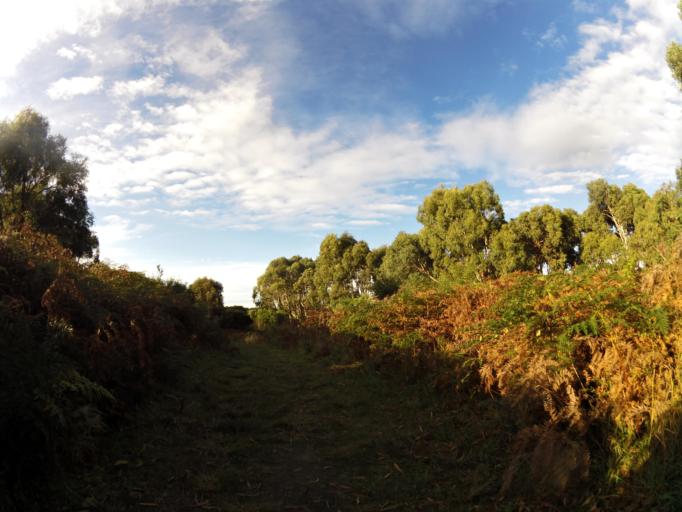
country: AU
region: Victoria
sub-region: Bass Coast
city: North Wonthaggi
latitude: -38.6043
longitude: 145.5621
